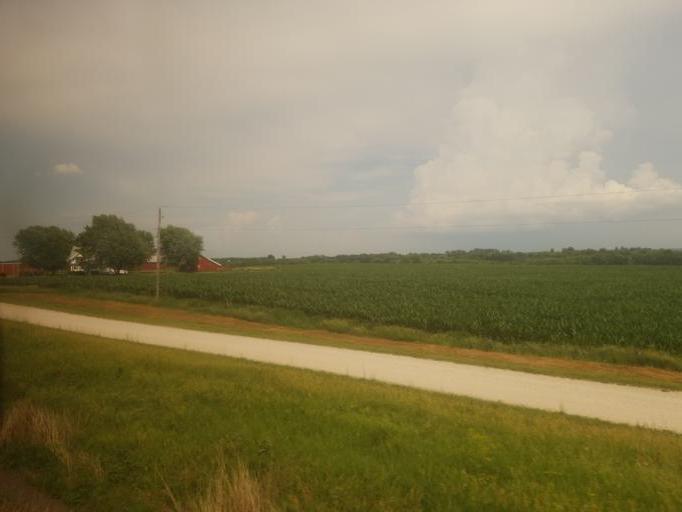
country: US
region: Illinois
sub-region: Henry County
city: Galva
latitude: 41.0986
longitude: -90.1857
